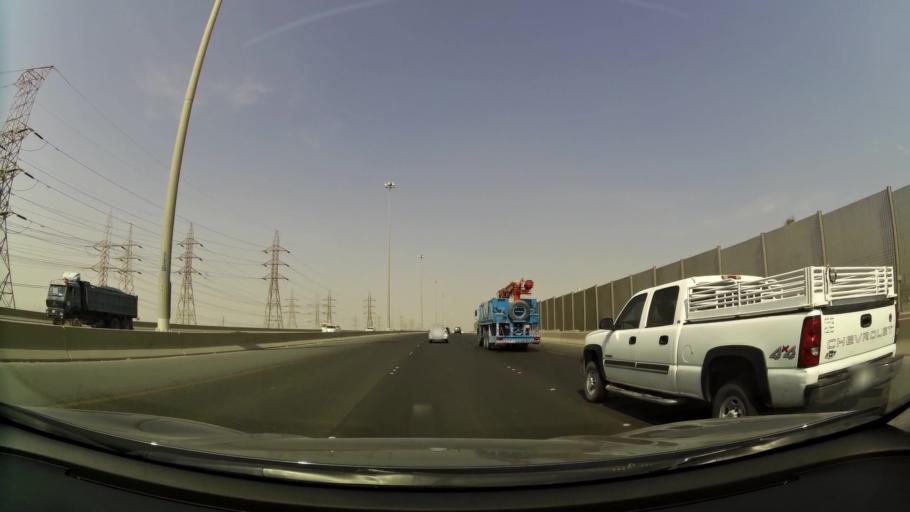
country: KW
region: Al Ahmadi
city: Al Fahahil
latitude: 29.0435
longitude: 48.1149
